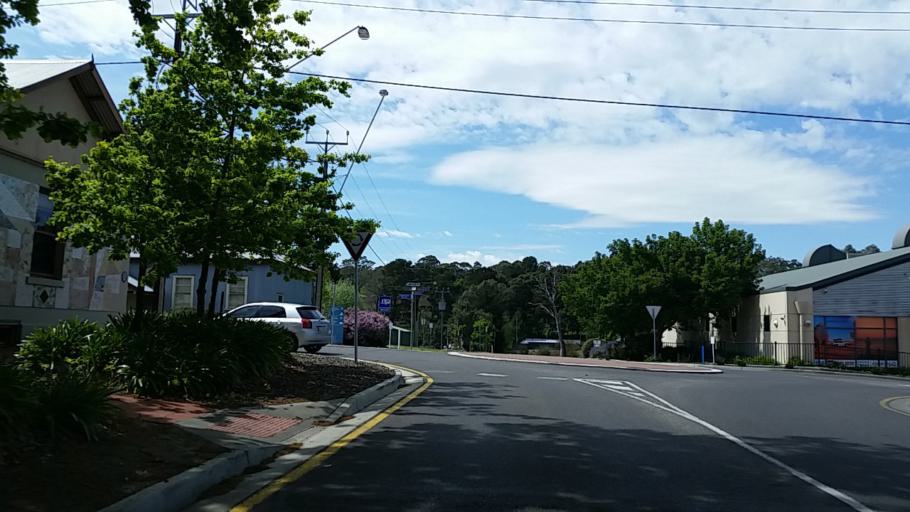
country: AU
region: South Australia
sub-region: Mount Barker
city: Mount Barker
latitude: -35.0633
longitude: 138.8598
